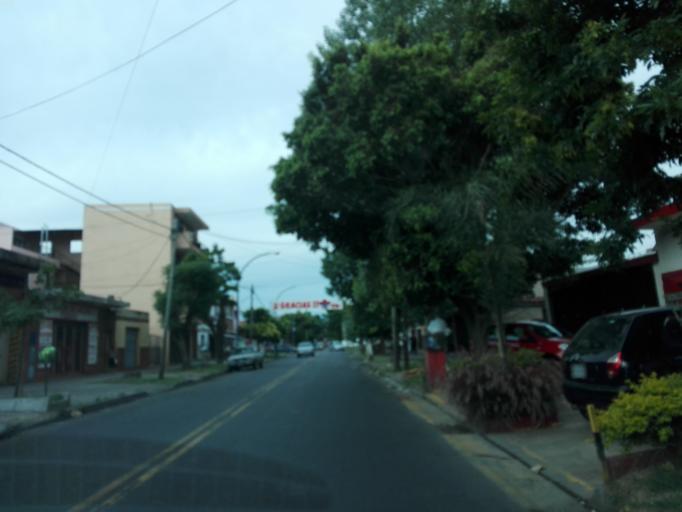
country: AR
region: Buenos Aires
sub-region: Partido de Lanus
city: Lanus
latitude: -34.7088
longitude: -58.3740
